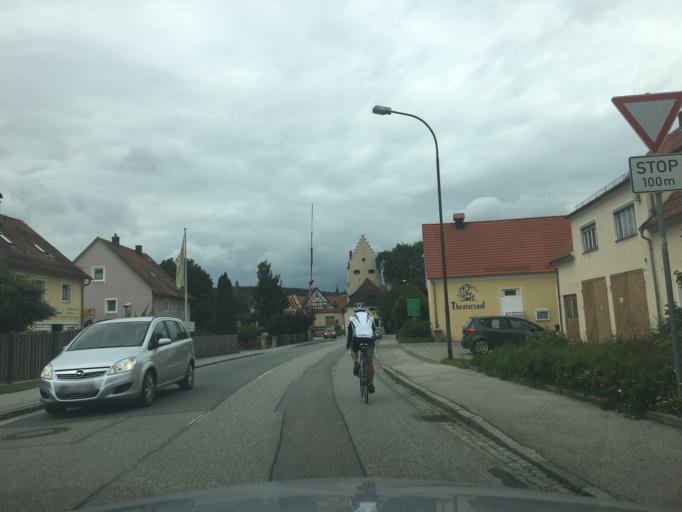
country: DE
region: Bavaria
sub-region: Regierungsbezirk Mittelfranken
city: Greding
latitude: 49.0453
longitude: 11.3578
